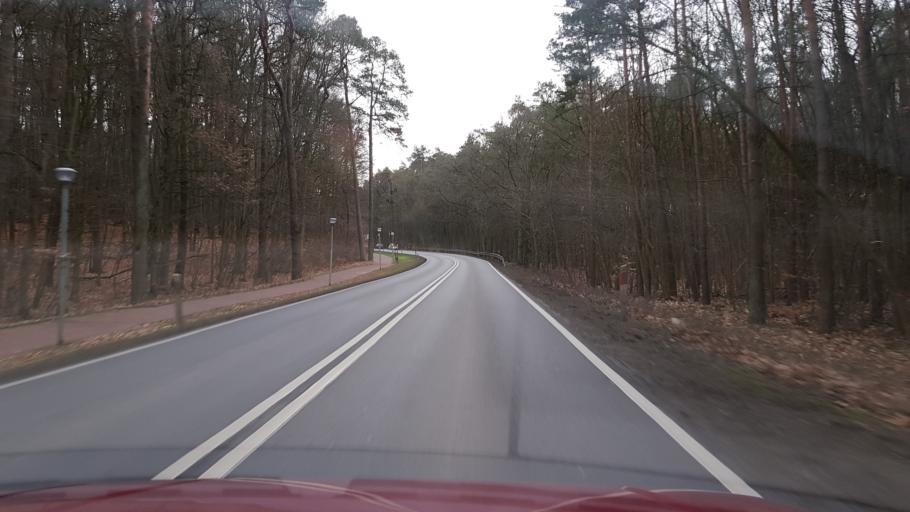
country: PL
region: West Pomeranian Voivodeship
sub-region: Szczecin
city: Szczecin
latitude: 53.4842
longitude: 14.4835
